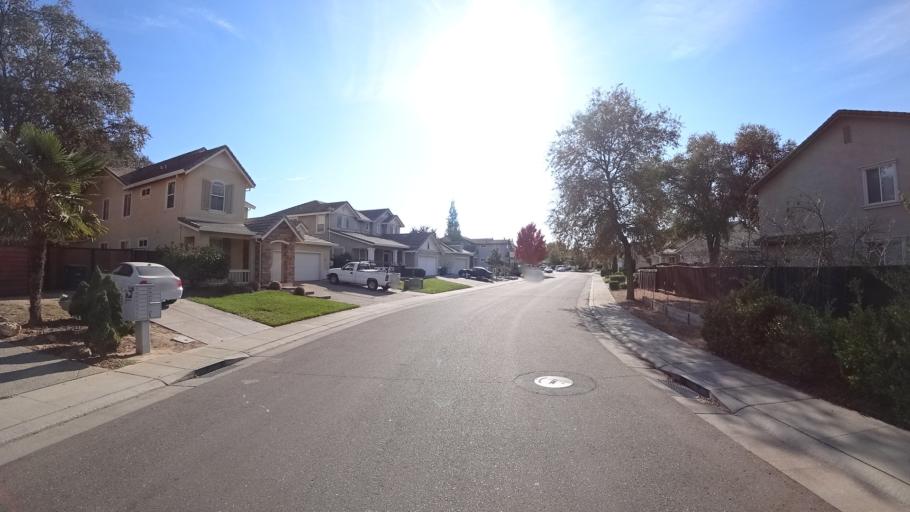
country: US
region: California
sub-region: Sacramento County
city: Citrus Heights
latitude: 38.6851
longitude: -121.2951
